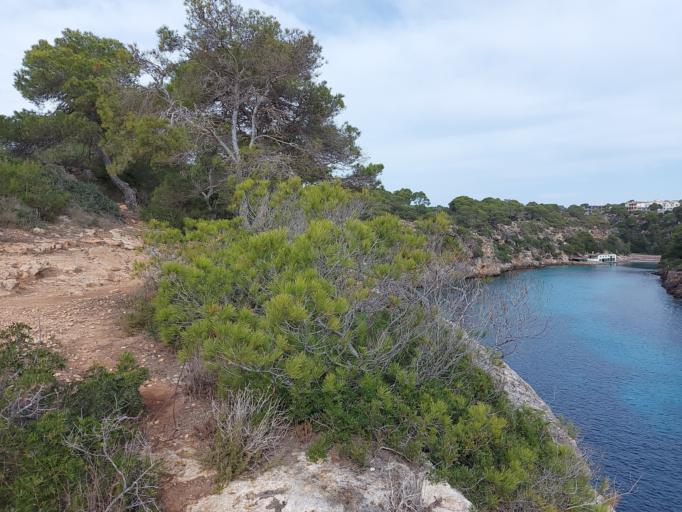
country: ES
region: Balearic Islands
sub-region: Illes Balears
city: Llucmajor
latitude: 39.3613
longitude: 2.8337
